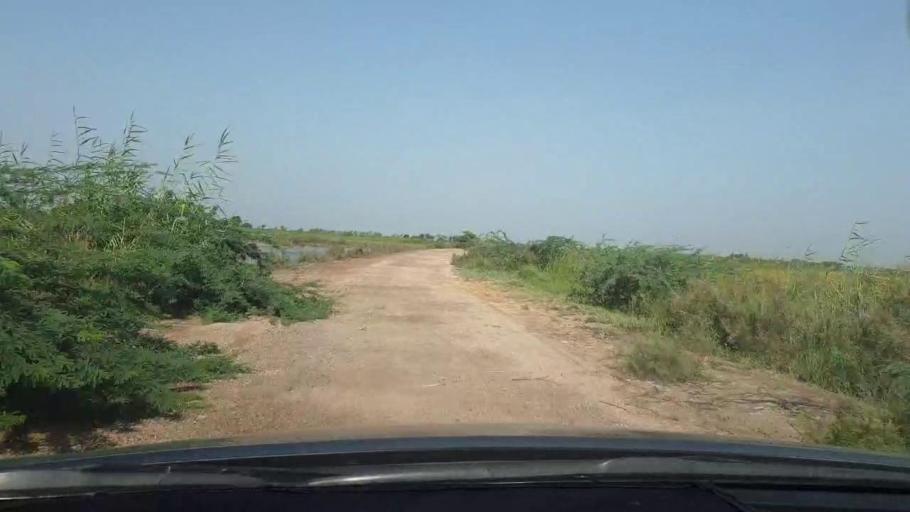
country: PK
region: Sindh
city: Tando Bago
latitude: 24.7100
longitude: 69.1089
